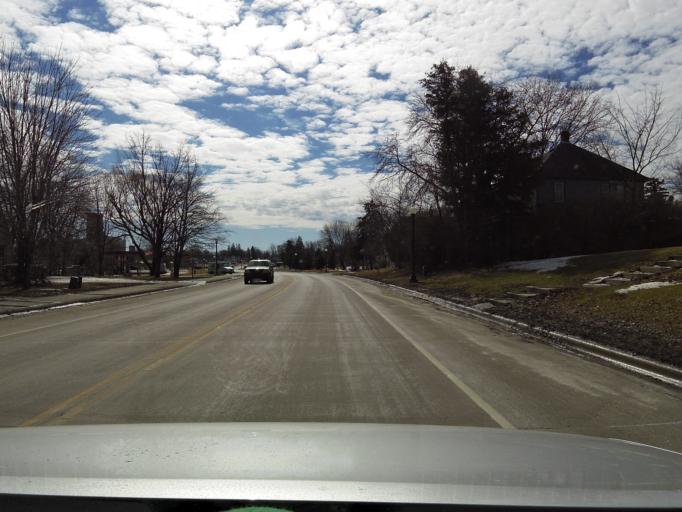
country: US
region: Minnesota
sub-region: Le Sueur County
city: New Prague
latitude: 44.5467
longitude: -93.5849
